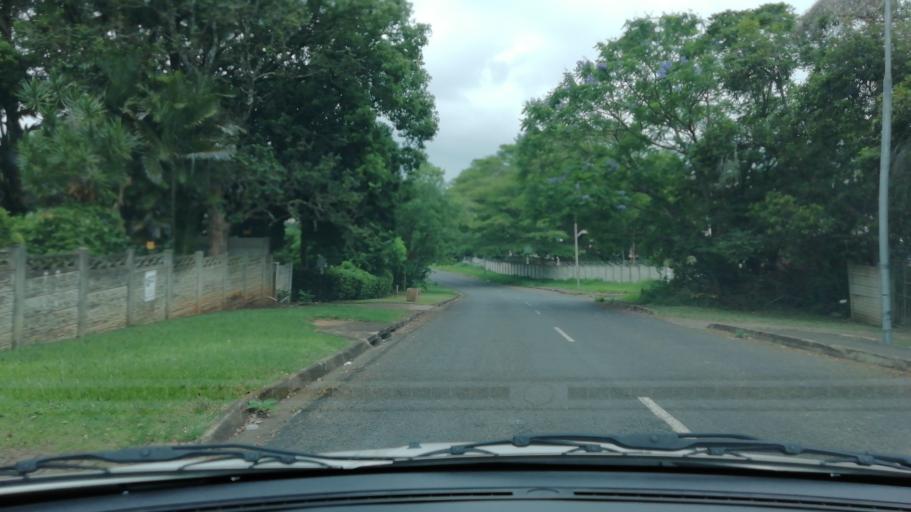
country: ZA
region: KwaZulu-Natal
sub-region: uThungulu District Municipality
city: Empangeni
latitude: -28.7390
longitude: 31.8988
